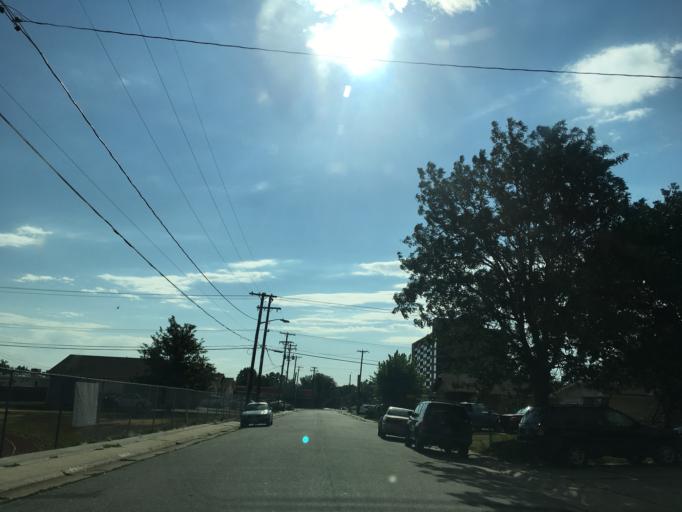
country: US
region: Colorado
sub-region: Arapahoe County
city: Sheridan
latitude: 39.6949
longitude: -105.0271
